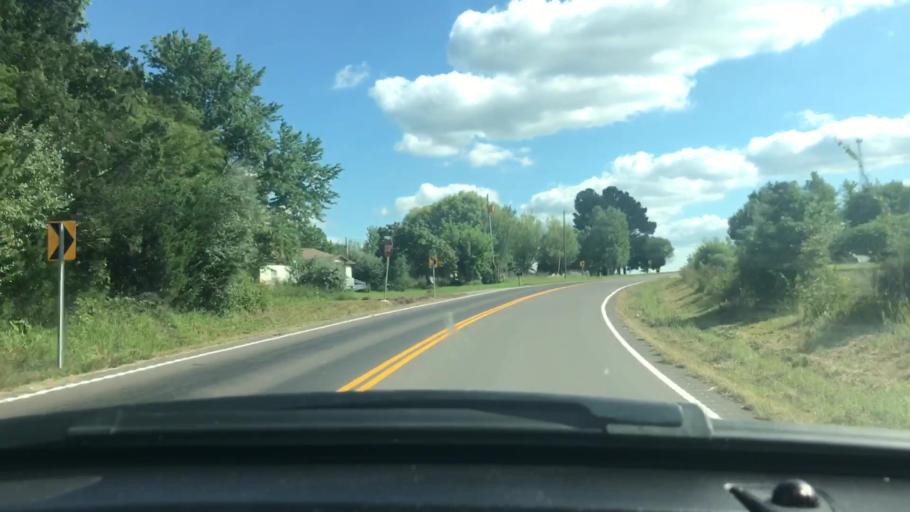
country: US
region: Missouri
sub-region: Wright County
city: Mountain Grove
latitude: 37.2527
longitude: -92.3005
